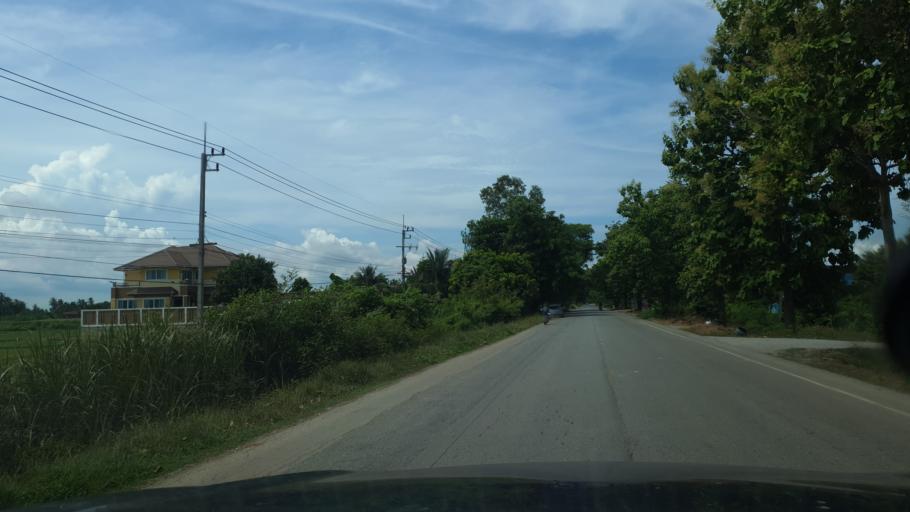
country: TH
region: Sukhothai
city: Sukhothai
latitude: 17.0686
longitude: 99.8305
